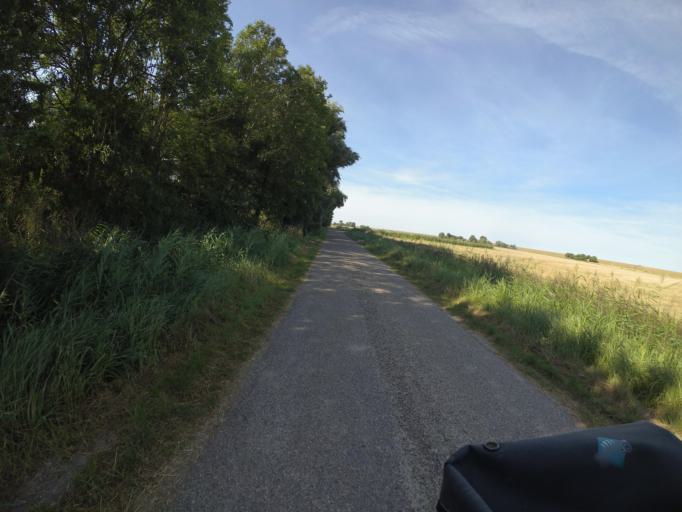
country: NL
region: Friesland
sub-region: Gemeente Ferwerderadiel
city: Marrum
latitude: 53.3409
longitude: 5.8038
